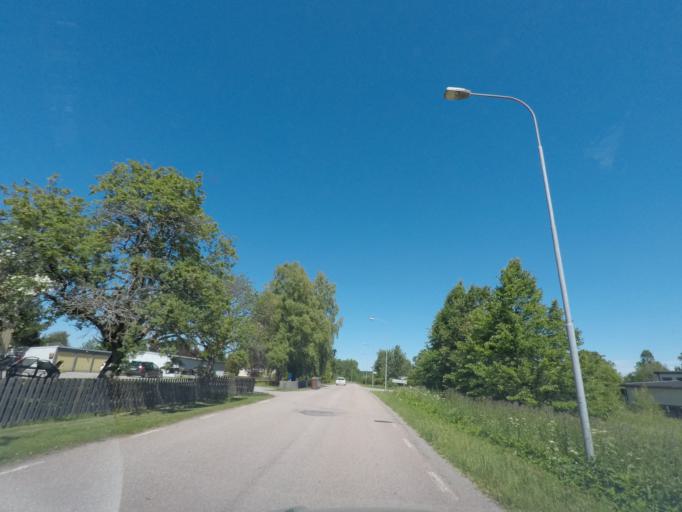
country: SE
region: Uppsala
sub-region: Enkopings Kommun
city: Irsta
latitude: 59.6773
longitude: 16.8381
